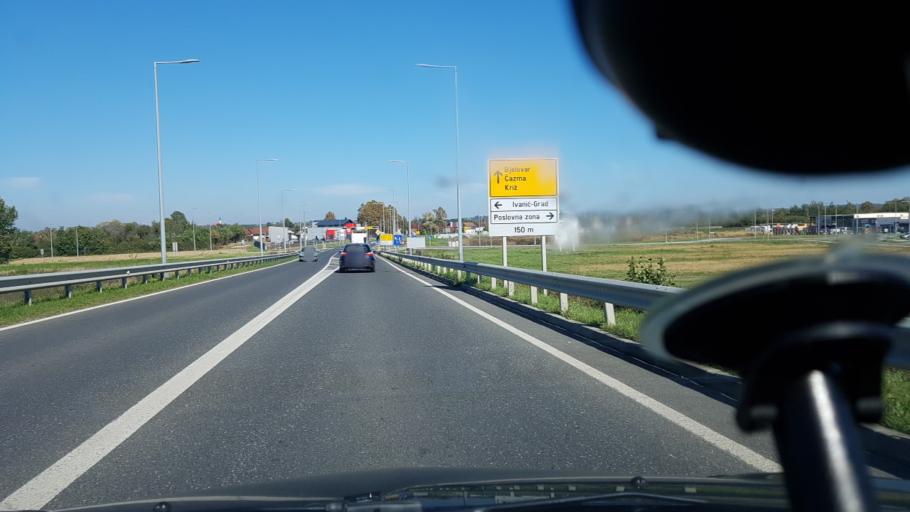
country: HR
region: Zagrebacka
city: Lupoglav
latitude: 45.7057
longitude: 16.4091
